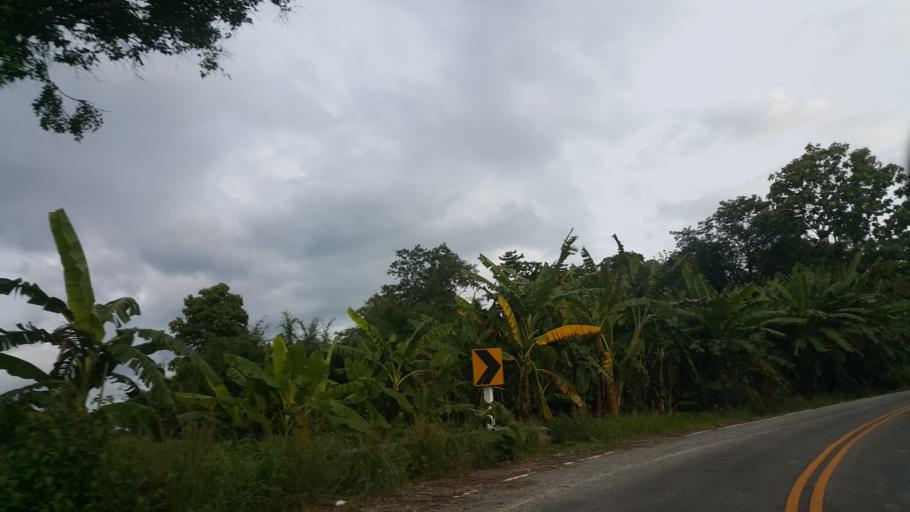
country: TH
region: Loei
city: Na Haeo
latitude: 17.4772
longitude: 101.1134
